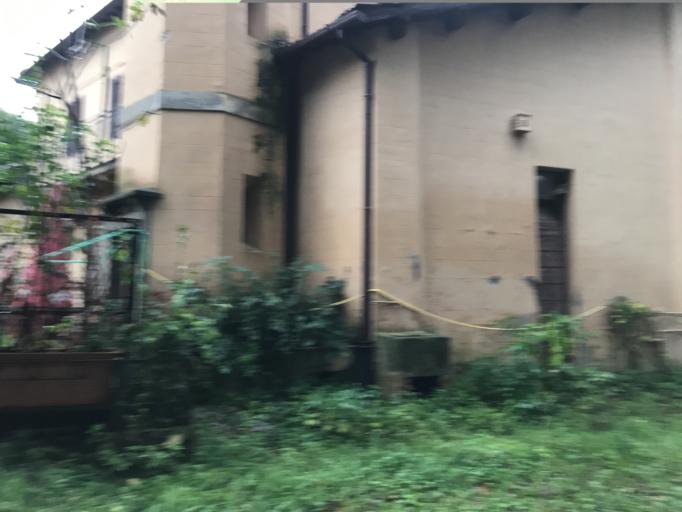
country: IT
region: Latium
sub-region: Citta metropolitana di Roma Capitale
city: Rome
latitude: 41.9137
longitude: 12.5098
